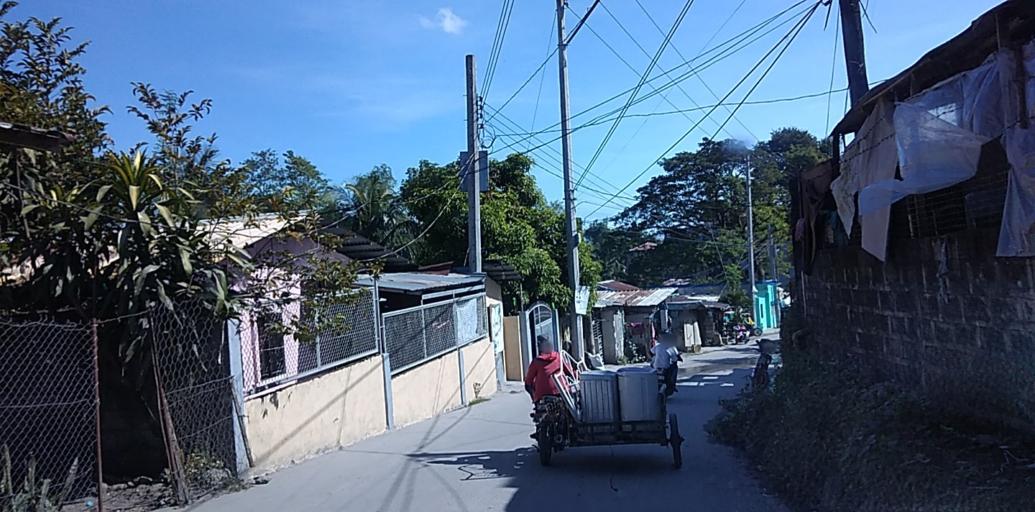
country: PH
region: Central Luzon
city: Santol
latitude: 15.1686
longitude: 120.5082
